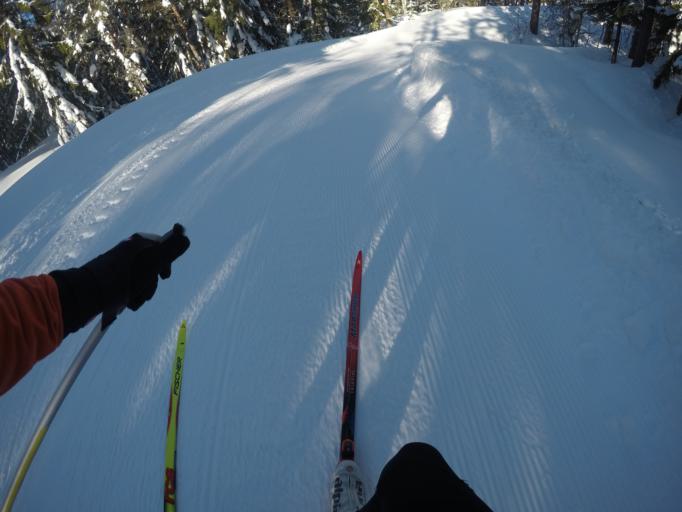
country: SE
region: Vaesternorrland
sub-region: Sundsvalls Kommun
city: Sundsvall
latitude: 62.3676
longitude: 17.2996
